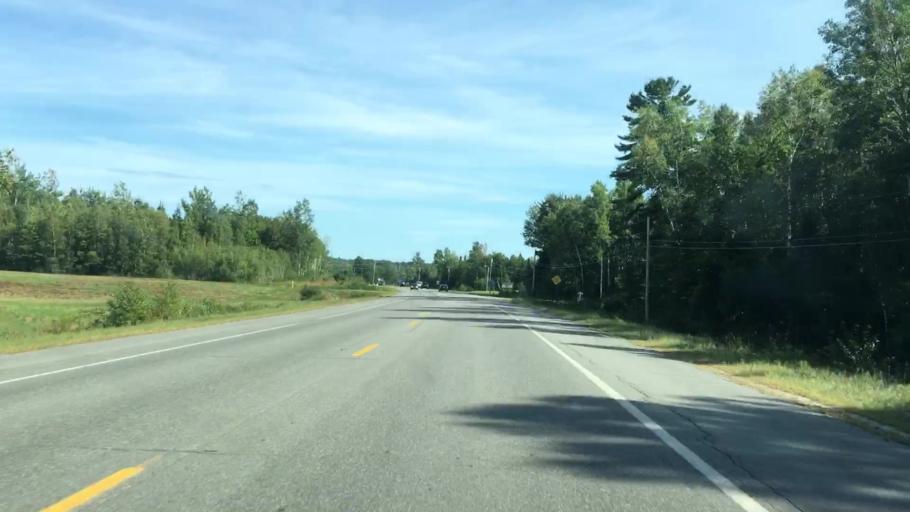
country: US
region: Maine
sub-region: Penobscot County
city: Lincoln
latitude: 45.3594
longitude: -68.5442
